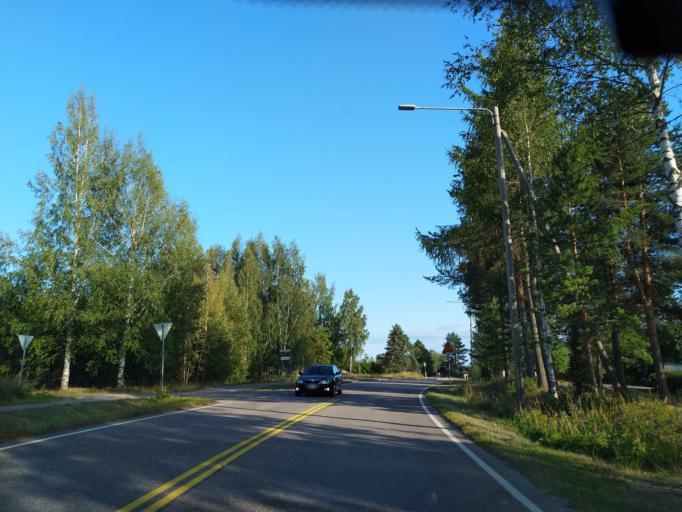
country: FI
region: Central Finland
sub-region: Jaemsae
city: Kuhmoinen
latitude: 61.5833
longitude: 25.1727
